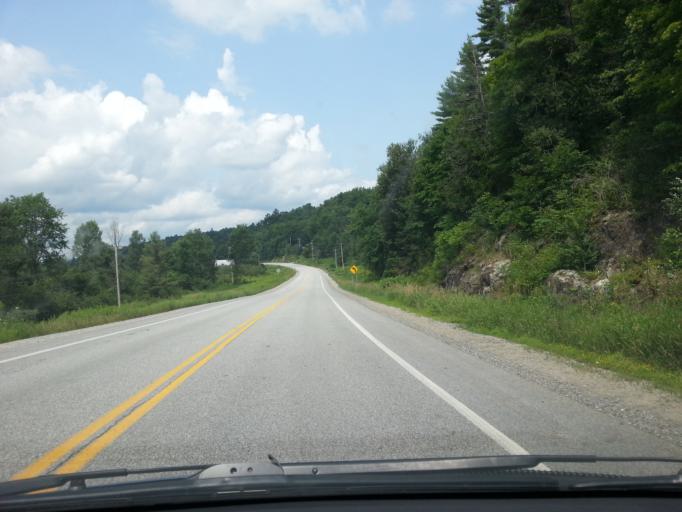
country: CA
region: Quebec
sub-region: Outaouais
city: Val-des-Monts
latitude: 45.6526
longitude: -75.6900
